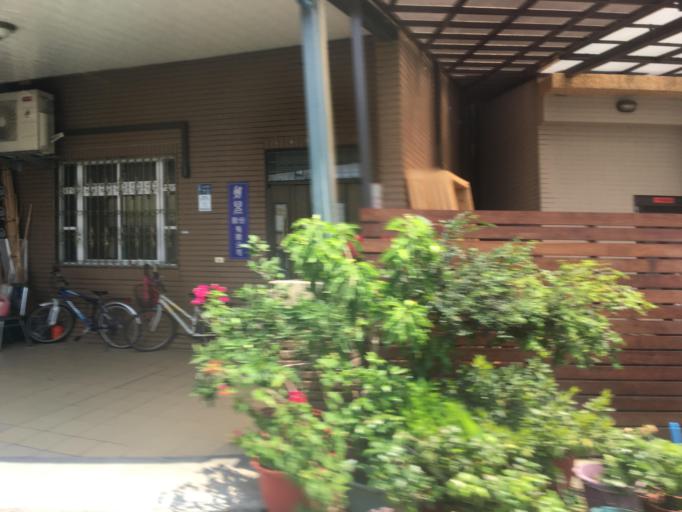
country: TW
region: Taiwan
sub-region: Yilan
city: Yilan
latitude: 24.6833
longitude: 121.7962
